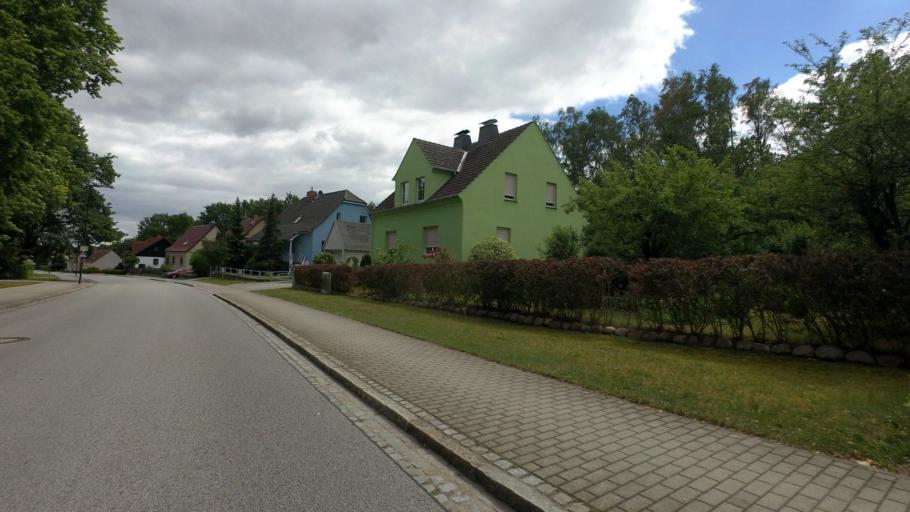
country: DE
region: Brandenburg
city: Luckau
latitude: 51.8513
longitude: 13.6984
